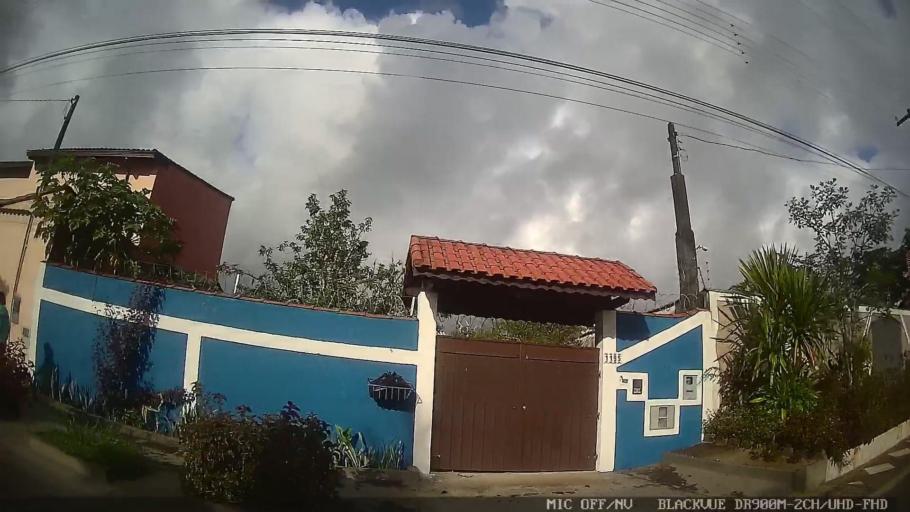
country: BR
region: Sao Paulo
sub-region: Itanhaem
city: Itanhaem
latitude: -24.1914
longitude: -46.8632
